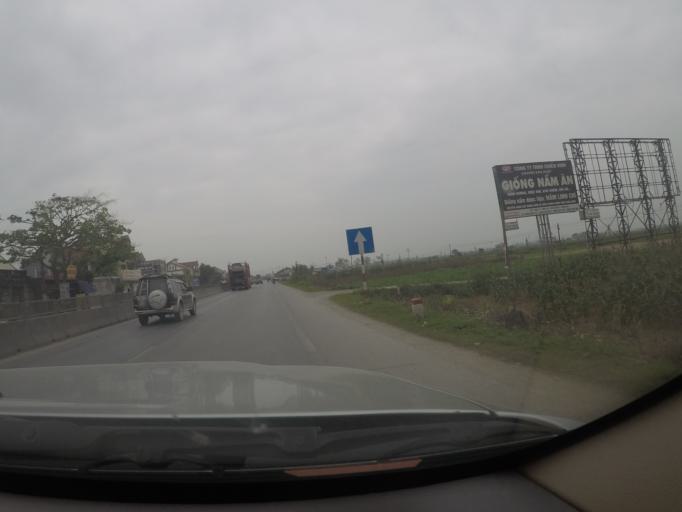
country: VN
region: Nghe An
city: Dien Chau
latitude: 19.0278
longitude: 105.5842
